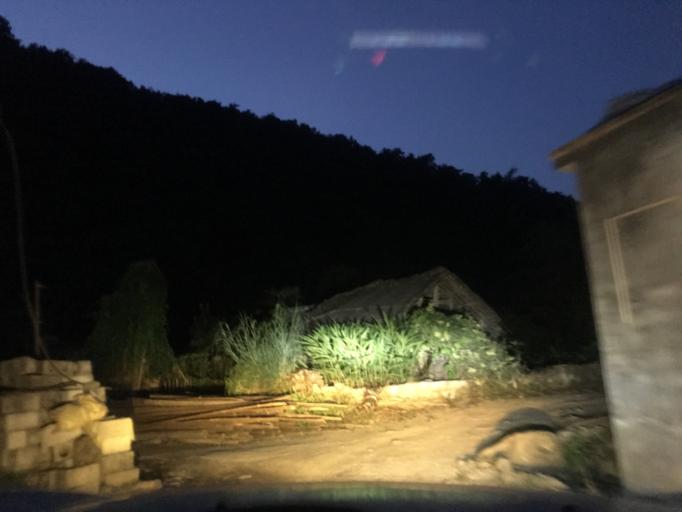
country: CN
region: Guangxi Zhuangzu Zizhiqu
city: Xinzhou
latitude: 25.3621
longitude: 105.7339
